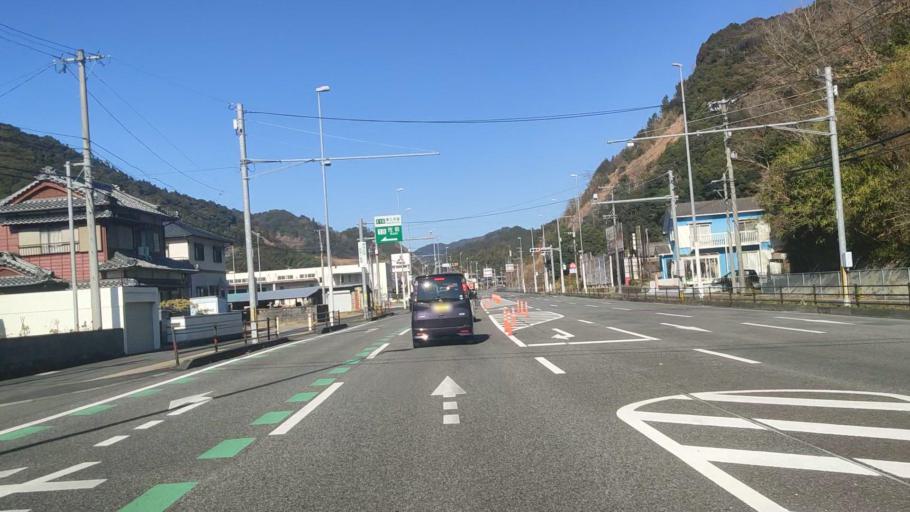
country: JP
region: Oita
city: Saiki
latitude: 32.9645
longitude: 131.8619
